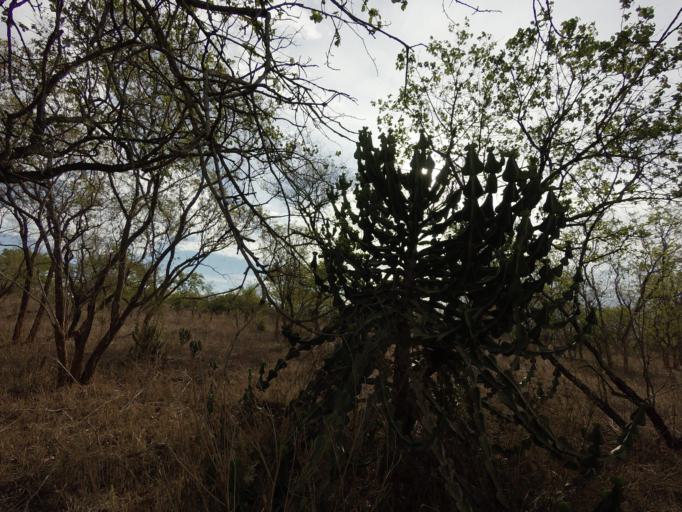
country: ZA
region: Limpopo
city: Thulamahashi
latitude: -24.5286
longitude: 31.1200
